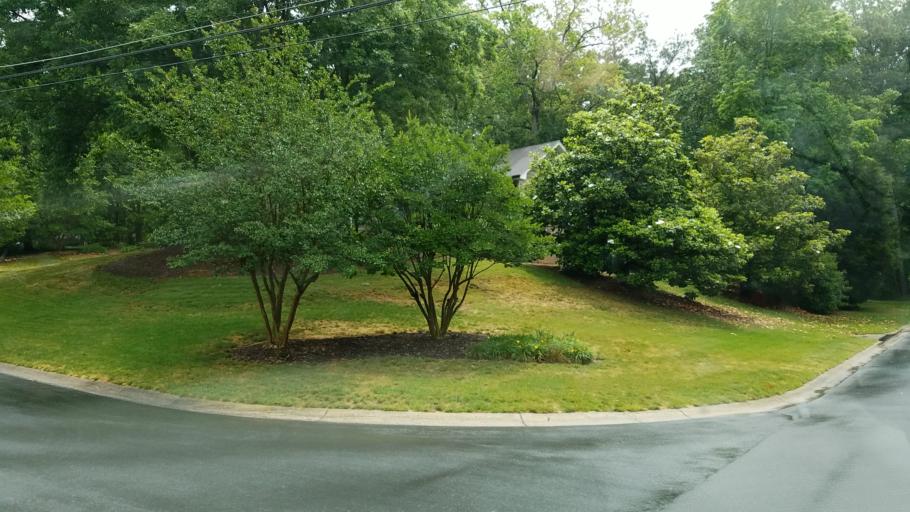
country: US
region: Georgia
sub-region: DeKalb County
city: Dunwoody
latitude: 33.9461
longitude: -84.3438
